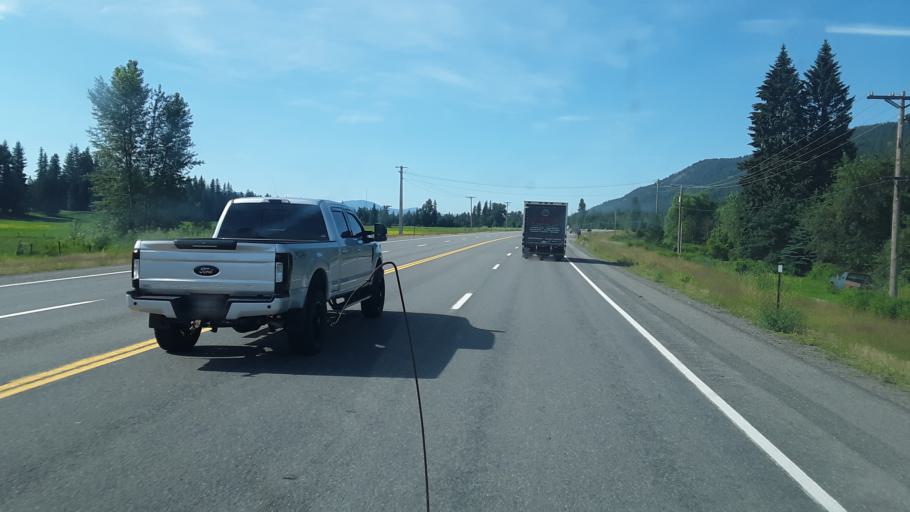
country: US
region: Idaho
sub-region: Bonner County
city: Ponderay
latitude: 48.3800
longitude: -116.5446
